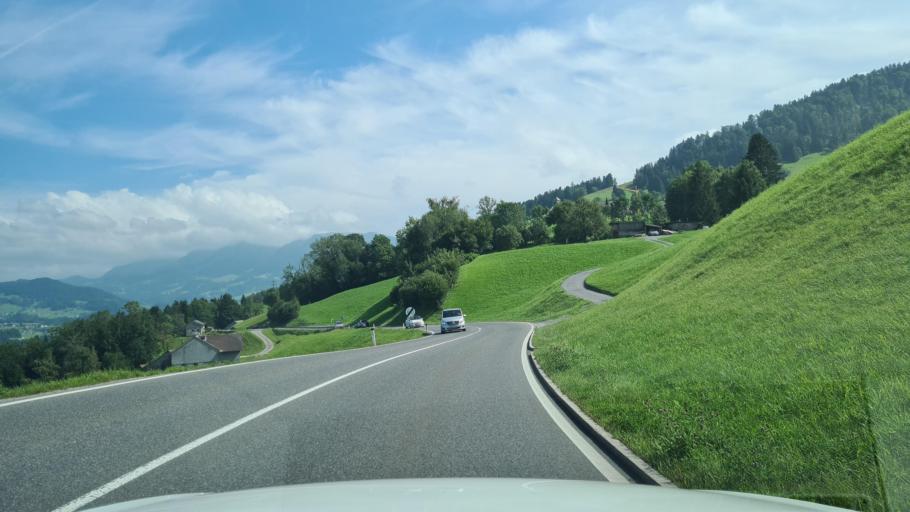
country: AT
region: Vorarlberg
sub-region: Politischer Bezirk Bregenz
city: Doren
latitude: 47.4621
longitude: 9.8556
